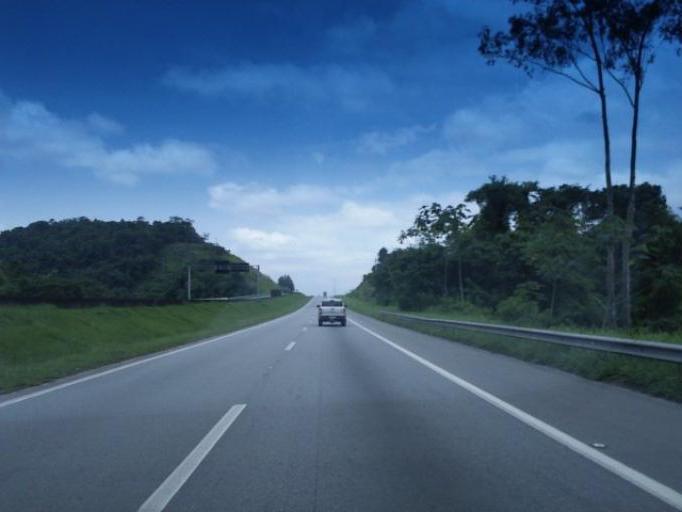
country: BR
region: Sao Paulo
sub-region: Miracatu
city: Miracatu
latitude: -24.1662
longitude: -47.3341
